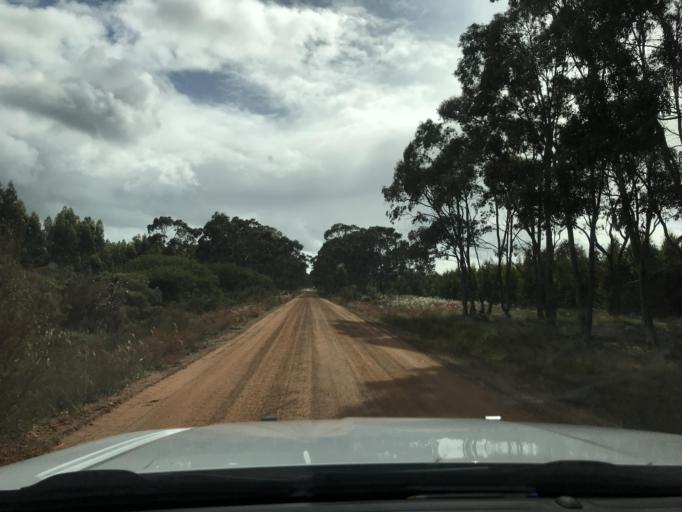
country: AU
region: South Australia
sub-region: Wattle Range
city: Penola
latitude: -37.1874
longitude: 141.1936
